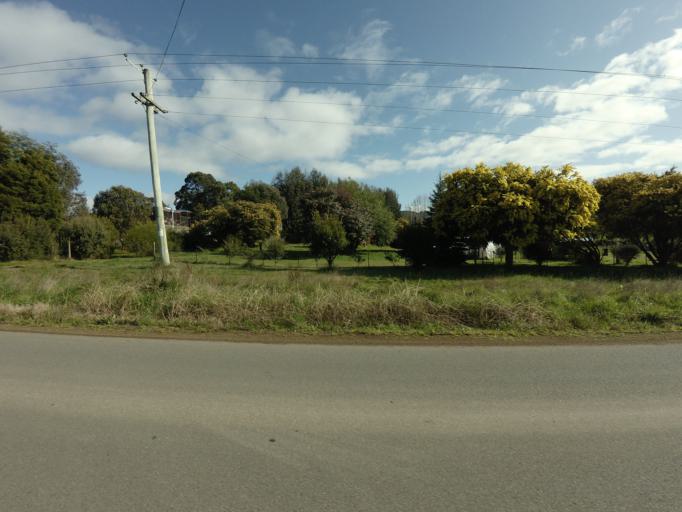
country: AU
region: Tasmania
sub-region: Huon Valley
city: Geeveston
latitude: -43.3247
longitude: 146.9929
